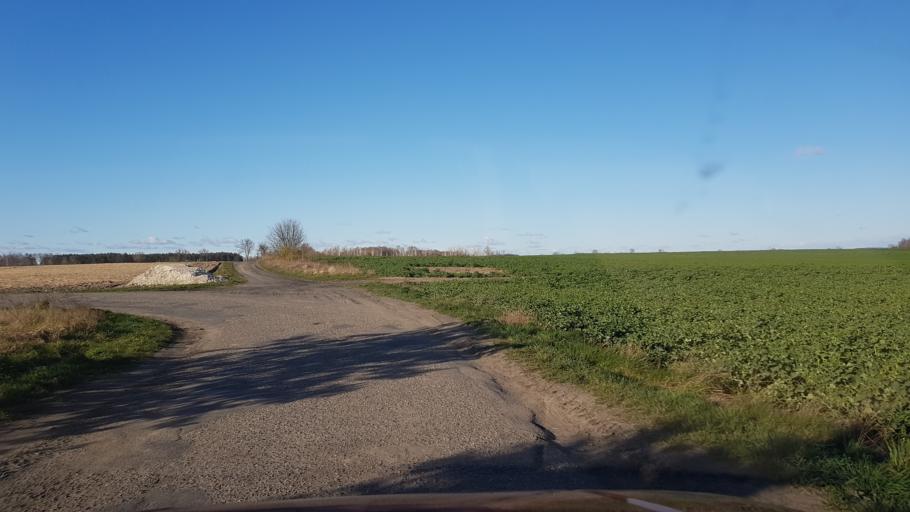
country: PL
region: West Pomeranian Voivodeship
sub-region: Powiat stargardzki
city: Stara Dabrowa
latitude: 53.3803
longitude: 15.1121
